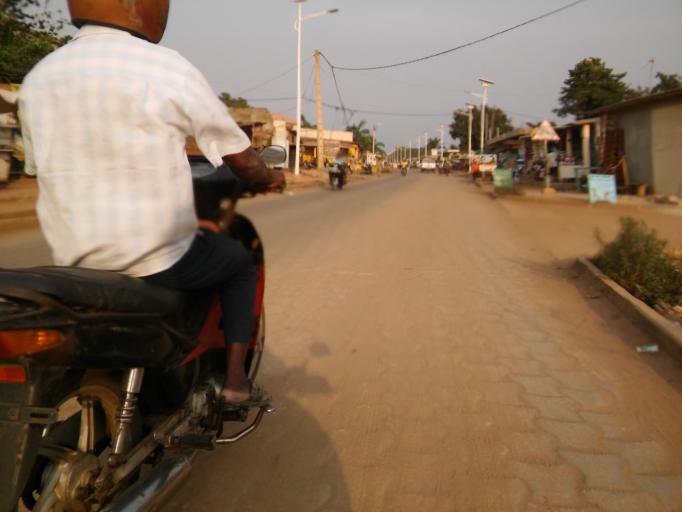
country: BJ
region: Atlantique
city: Abomey-Calavi
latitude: 6.4020
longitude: 2.3282
